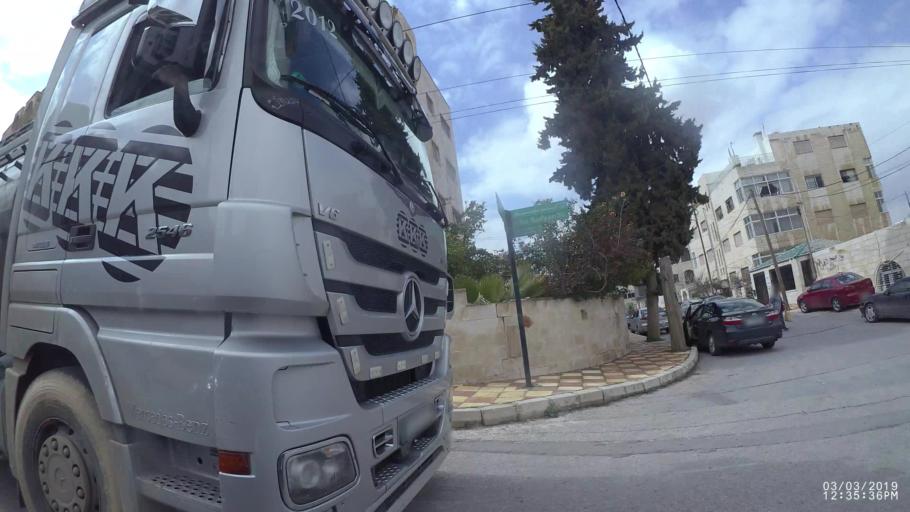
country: JO
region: Amman
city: Amman
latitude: 31.9757
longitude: 35.9028
